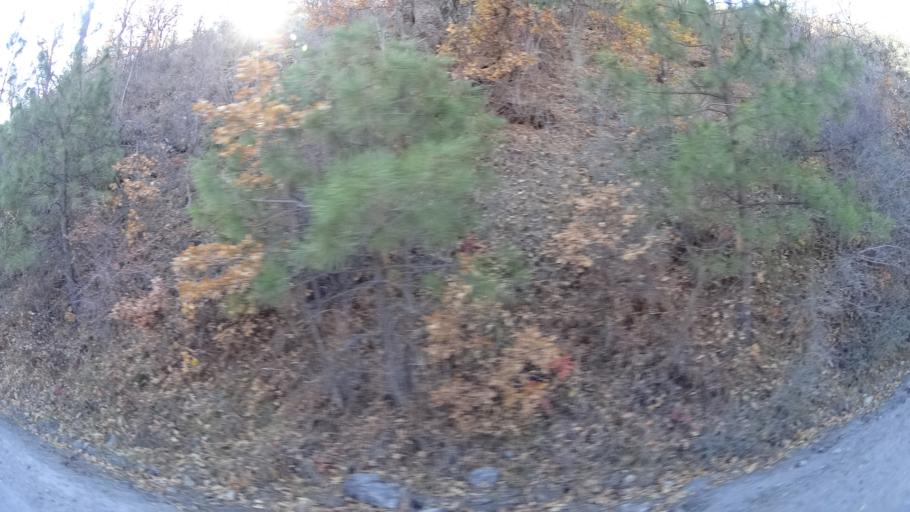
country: US
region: California
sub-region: Siskiyou County
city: Yreka
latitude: 41.7905
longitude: -122.6089
